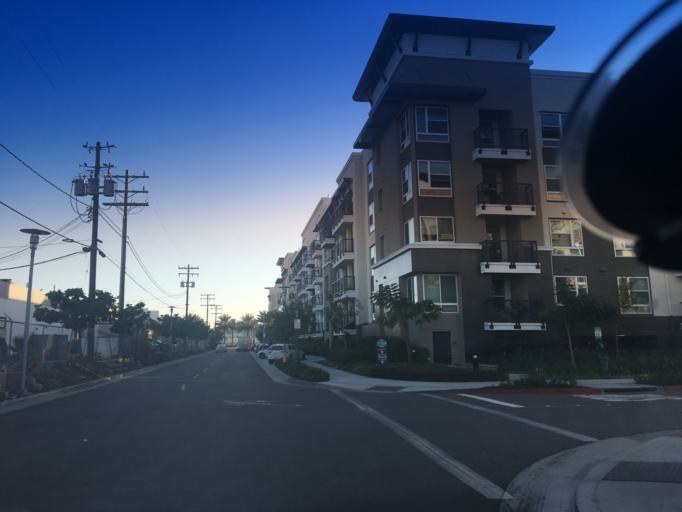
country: US
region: California
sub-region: Orange County
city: Anaheim
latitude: 33.8050
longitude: -117.8919
